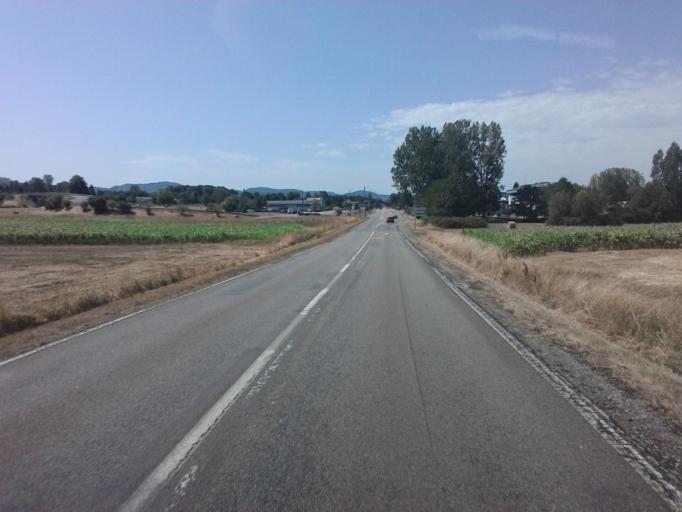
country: FR
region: Franche-Comte
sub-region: Departement du Jura
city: Montmorot
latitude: 46.6452
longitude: 5.5042
